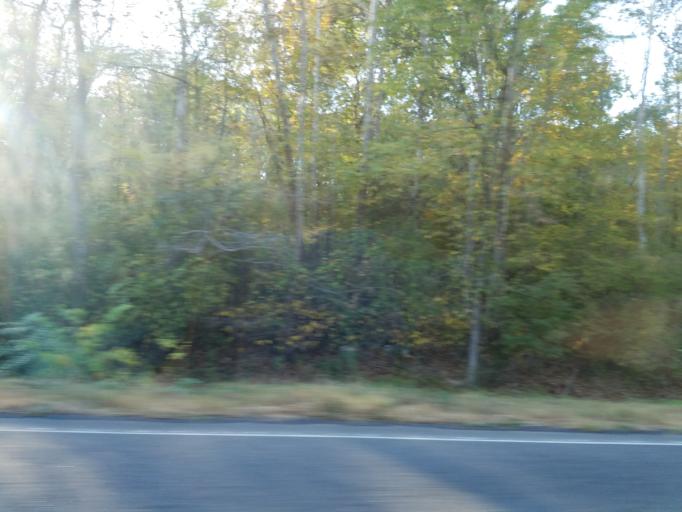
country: US
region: Georgia
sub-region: Bartow County
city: Adairsville
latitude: 34.2617
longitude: -84.9591
